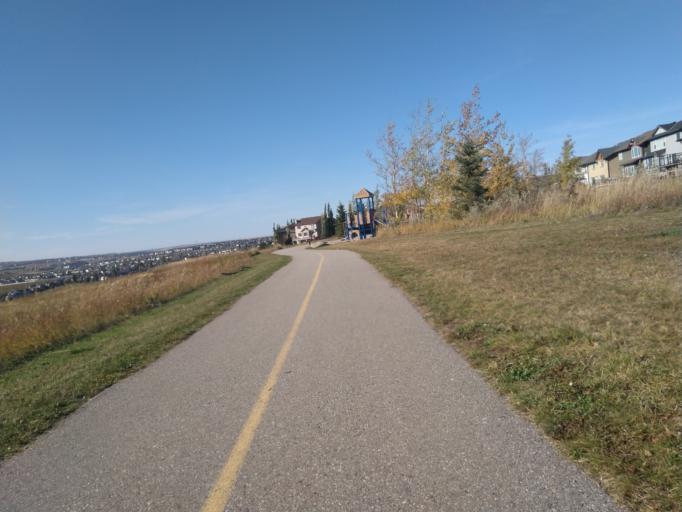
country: CA
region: Alberta
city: Calgary
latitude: 51.1549
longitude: -114.0935
